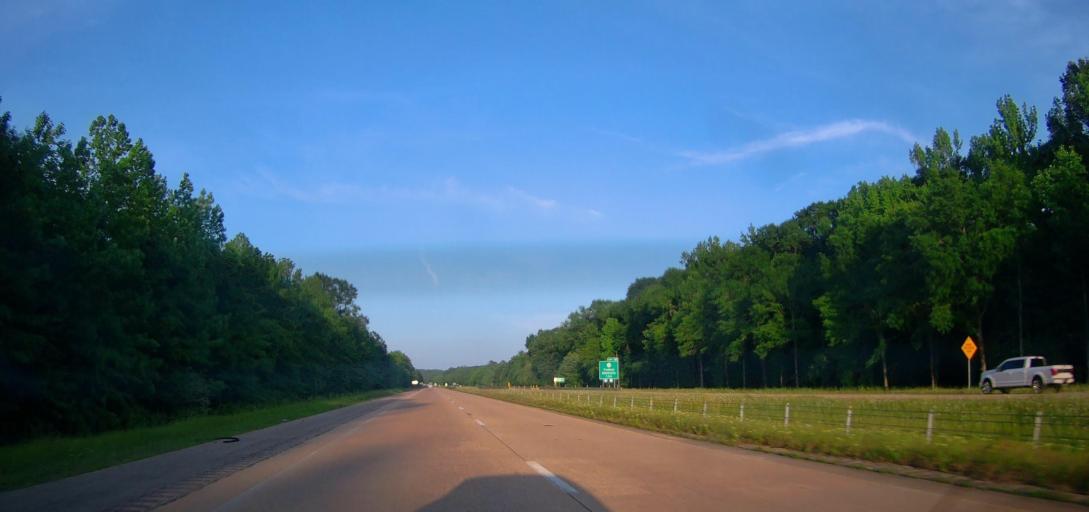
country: US
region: Mississippi
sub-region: Itawamba County
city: Fulton
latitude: 34.2216
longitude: -88.2843
